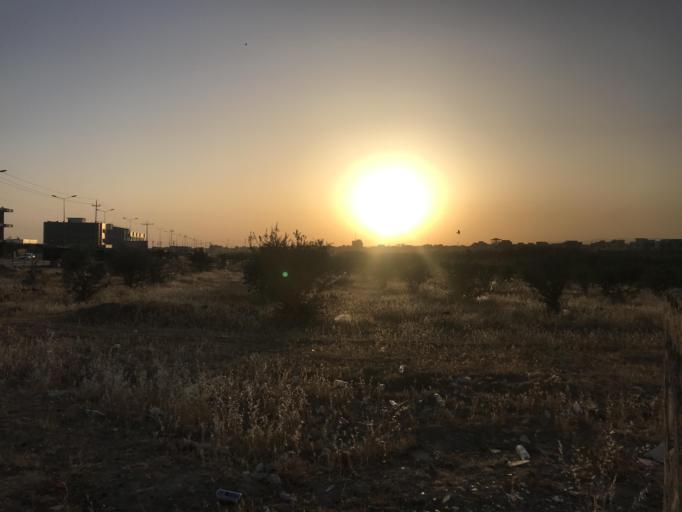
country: IQ
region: Dahuk
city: Saymayl
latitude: 36.8596
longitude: 42.8324
